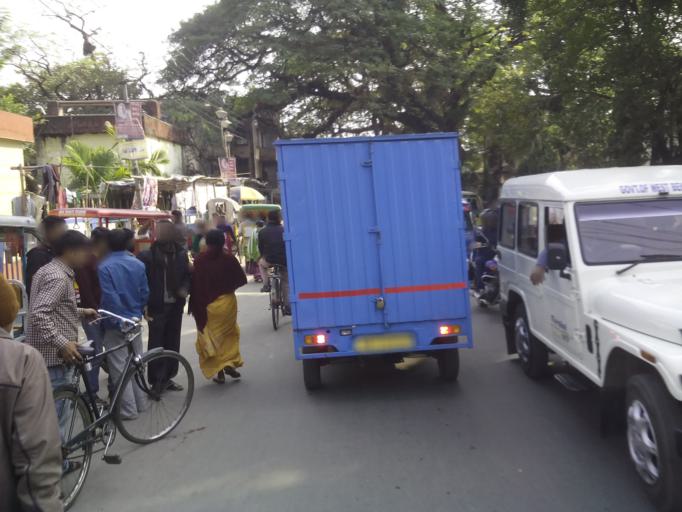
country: IN
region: West Bengal
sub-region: Darjiling
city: Shiliguri
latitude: 26.7106
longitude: 88.4277
